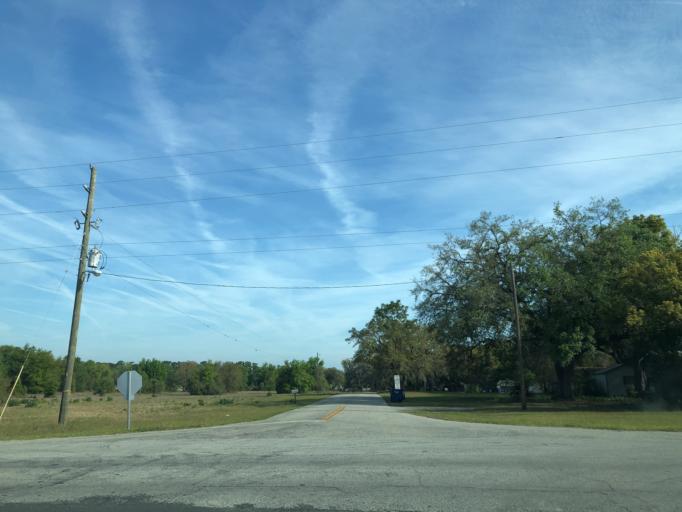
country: US
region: Florida
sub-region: Lake County
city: Astatula
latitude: 28.7208
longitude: -81.7331
